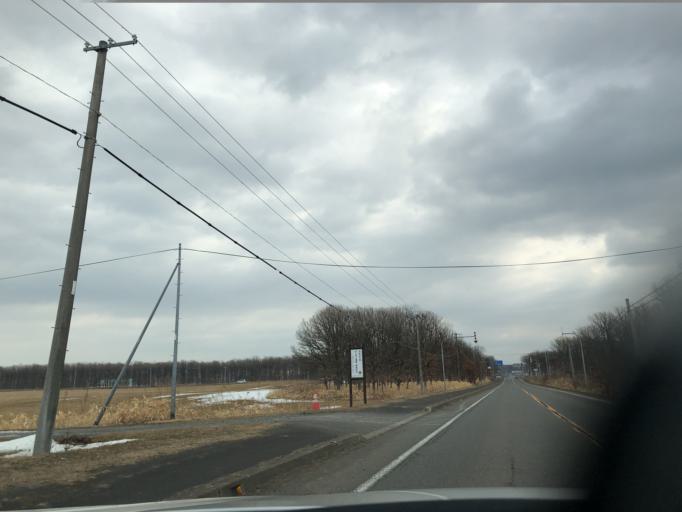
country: JP
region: Hokkaido
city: Chitose
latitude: 42.7606
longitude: 141.7500
